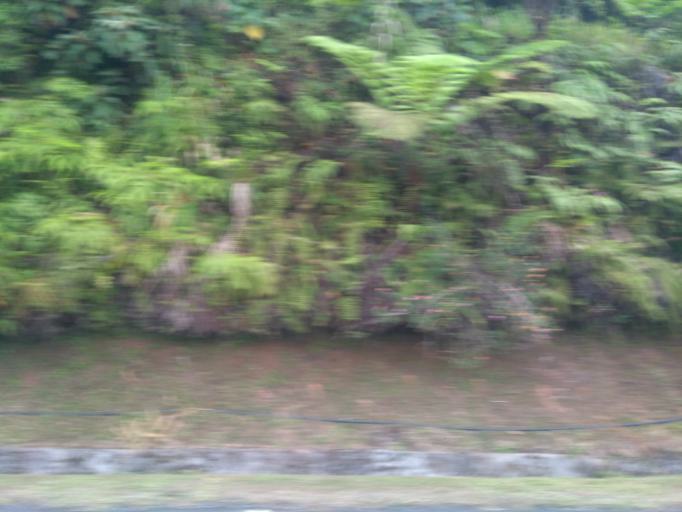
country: MY
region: Pahang
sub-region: Cameron Highlands
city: Tanah Rata
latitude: 4.5259
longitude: 101.4283
